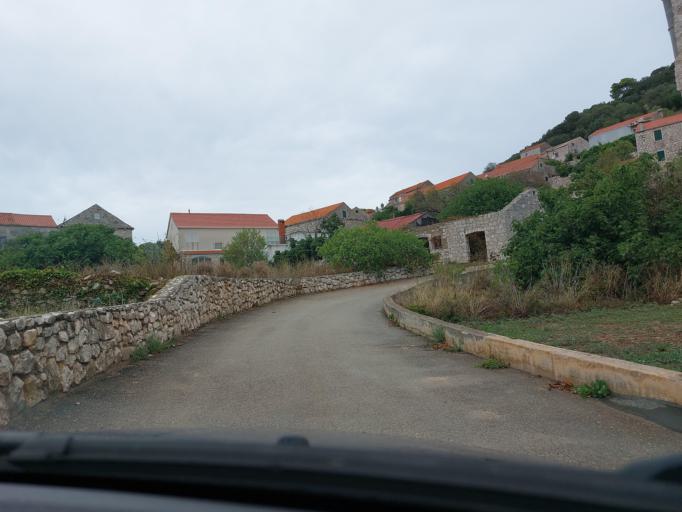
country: HR
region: Dubrovacko-Neretvanska
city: Smokvica
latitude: 42.7660
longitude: 16.9007
